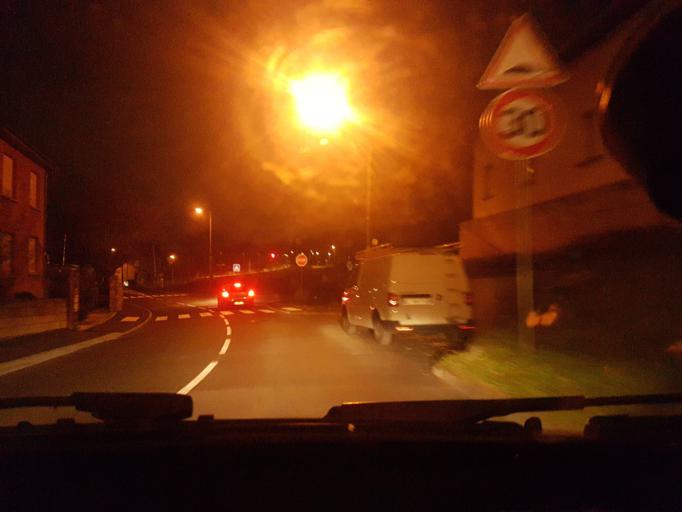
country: FR
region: Franche-Comte
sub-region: Territoire de Belfort
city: Danjoutin
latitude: 47.6167
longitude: 6.8700
